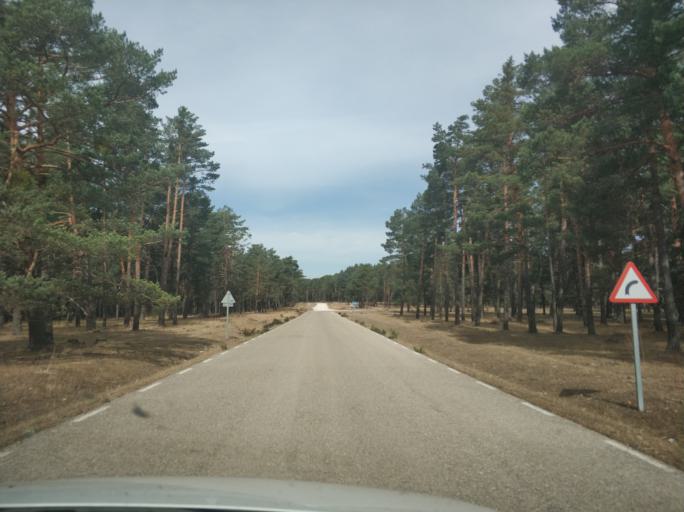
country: ES
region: Castille and Leon
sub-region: Provincia de Soria
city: Navaleno
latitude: 41.8669
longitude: -2.9440
